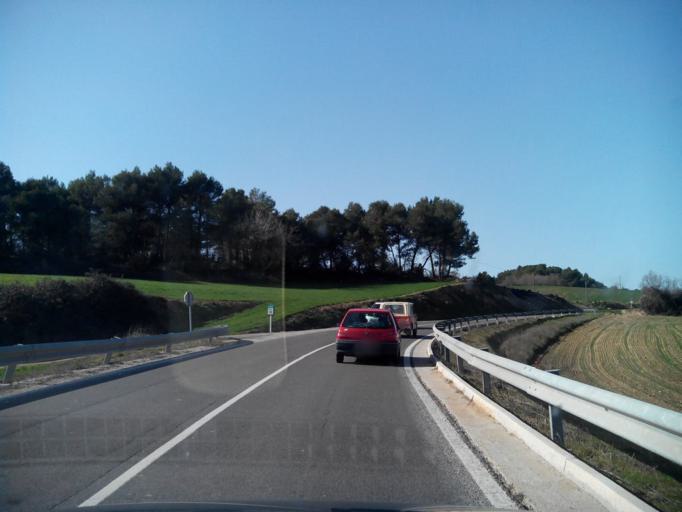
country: ES
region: Catalonia
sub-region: Provincia de Tarragona
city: Conesa
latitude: 41.4954
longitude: 1.3307
